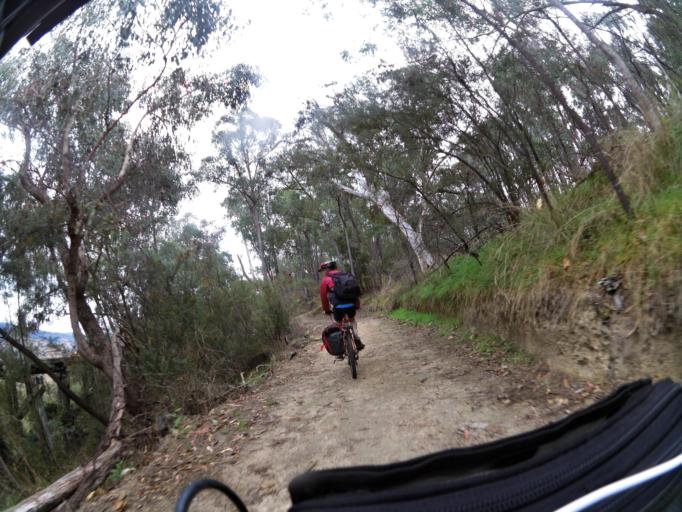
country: AU
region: New South Wales
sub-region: Greater Hume Shire
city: Holbrook
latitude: -36.1706
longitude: 147.4047
